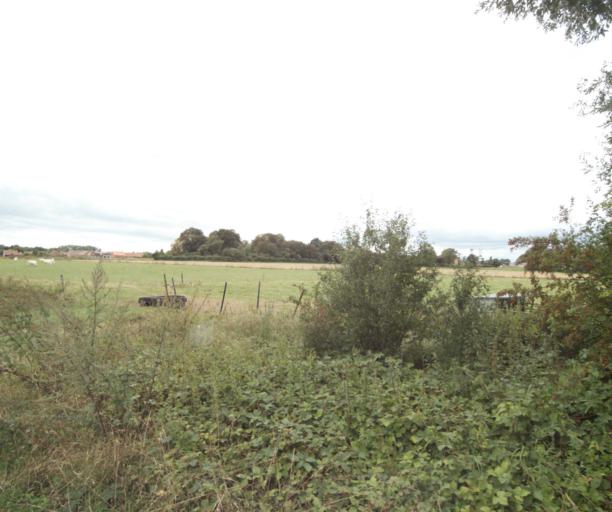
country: FR
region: Nord-Pas-de-Calais
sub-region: Departement du Nord
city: Sainghin-en-Melantois
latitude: 50.5660
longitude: 3.1787
